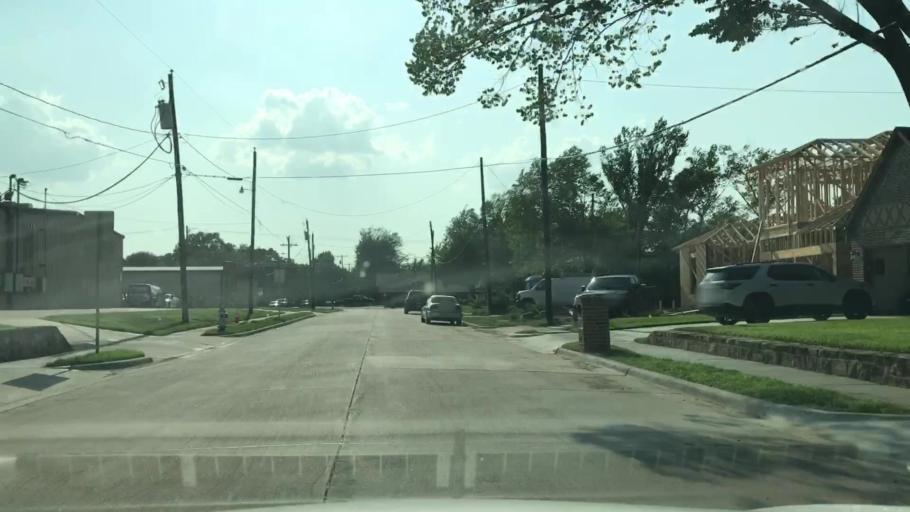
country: US
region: Texas
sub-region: Dallas County
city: Irving
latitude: 32.8199
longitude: -96.9410
